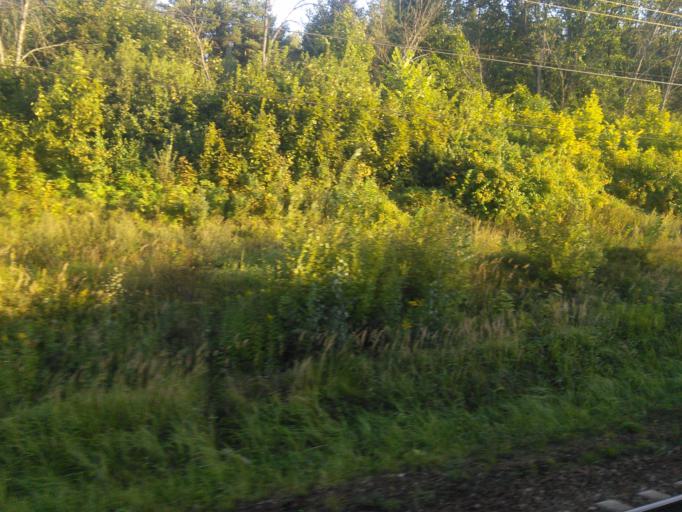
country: RU
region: Moskovskaya
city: Rakhmanovo
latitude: 55.7674
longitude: 38.6213
